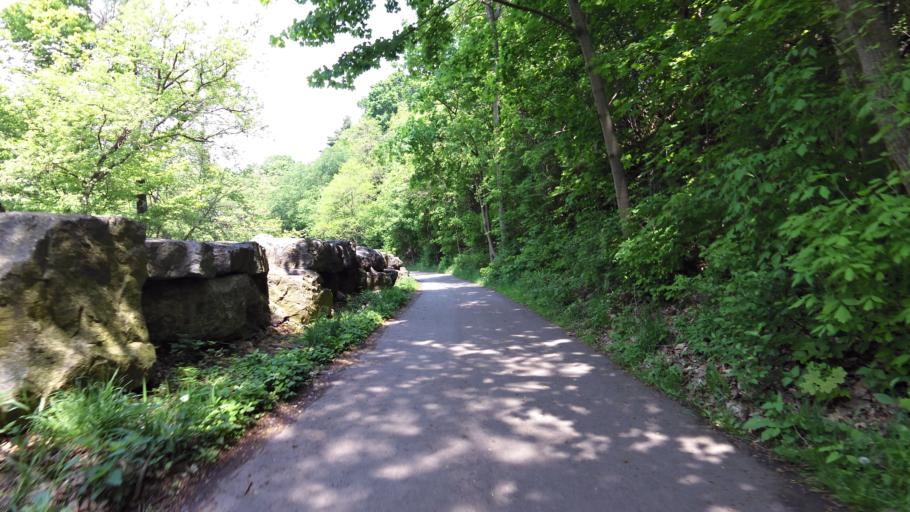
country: CA
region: Ontario
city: Etobicoke
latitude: 43.5941
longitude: -79.5485
